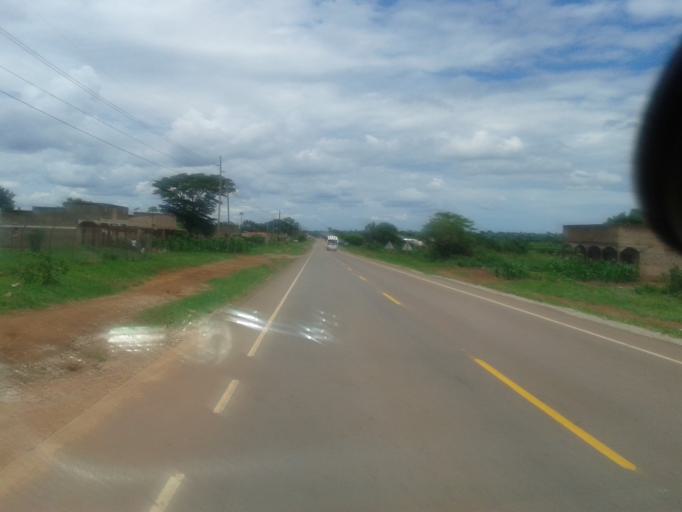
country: UG
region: Western Region
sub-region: Kiryandongo District
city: Kiryandongo
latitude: 1.7975
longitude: 32.0114
